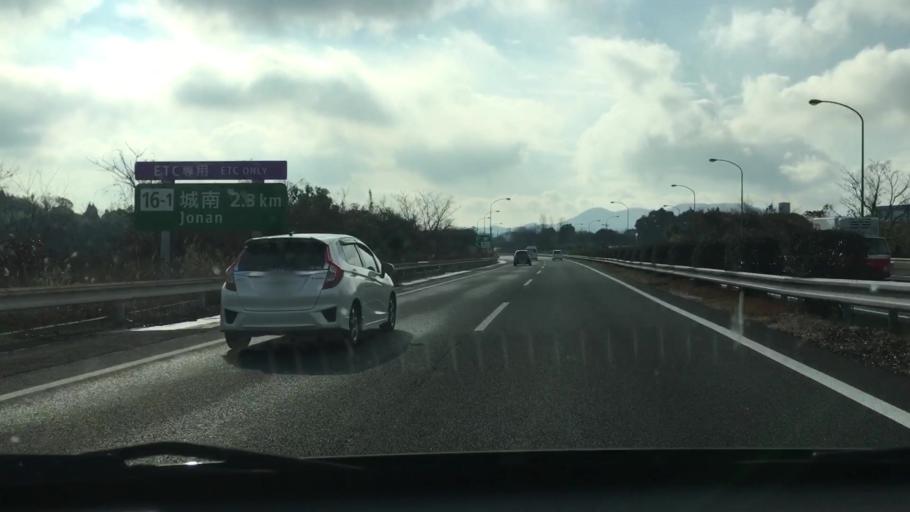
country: JP
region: Kumamoto
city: Uto
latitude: 32.7101
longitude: 130.7602
